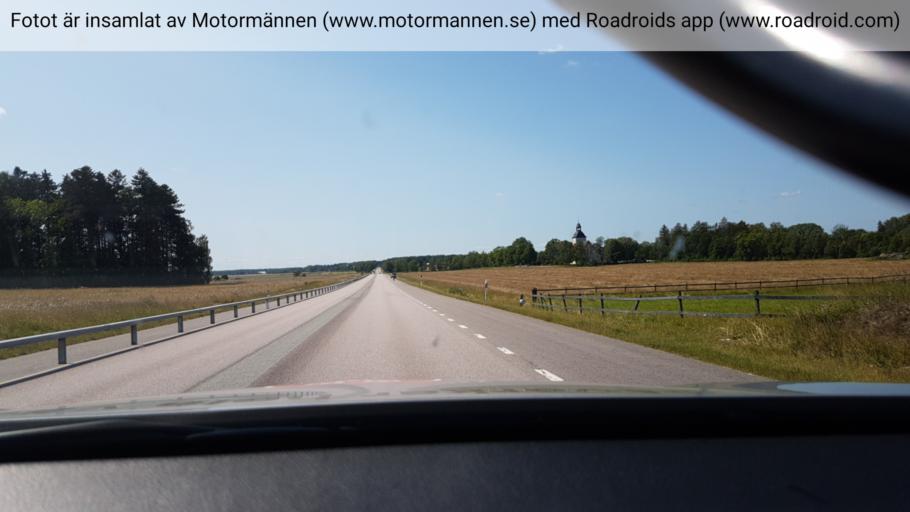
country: SE
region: Uppsala
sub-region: Enkopings Kommun
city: Hummelsta
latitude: 59.6332
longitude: 17.0005
